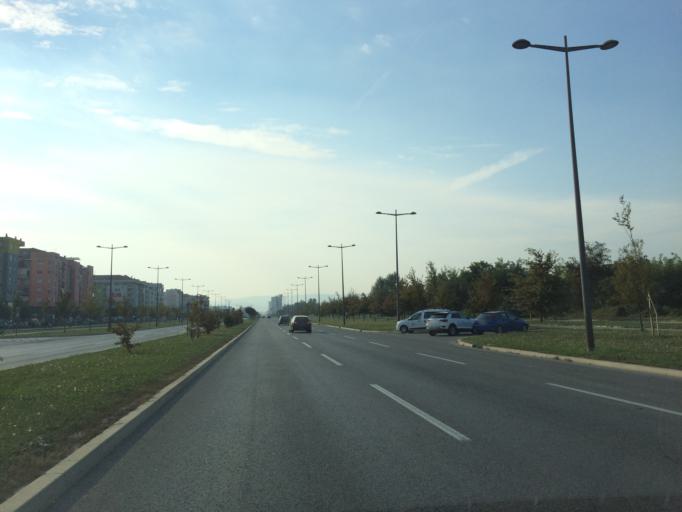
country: RS
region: Autonomna Pokrajina Vojvodina
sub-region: Juznobacki Okrug
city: Novi Sad
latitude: 45.2592
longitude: 19.8092
